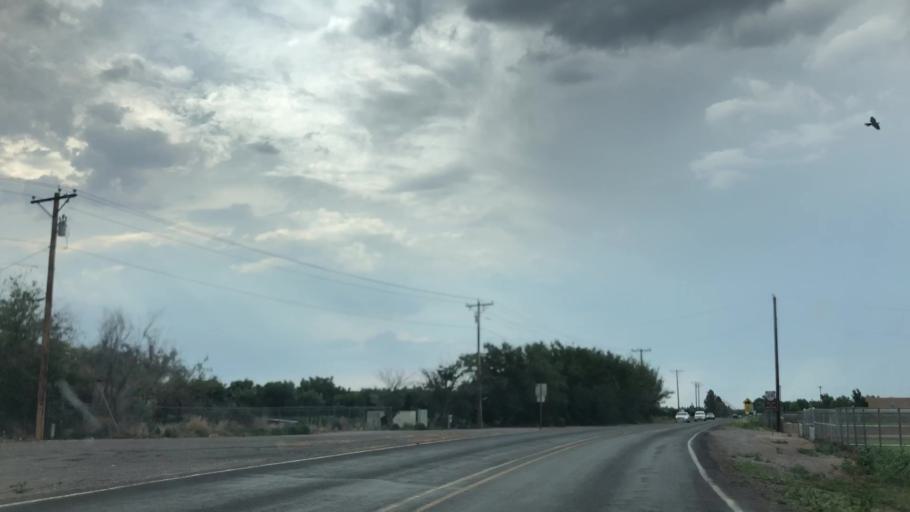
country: US
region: Texas
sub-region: El Paso County
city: Canutillo
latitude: 31.9199
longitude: -106.6264
